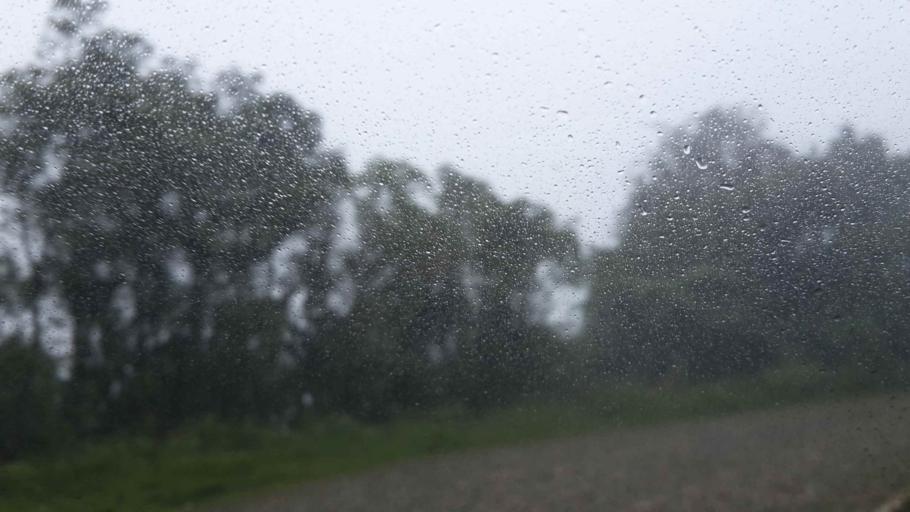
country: BO
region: Cochabamba
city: Colomi
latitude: -17.1697
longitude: -65.8956
